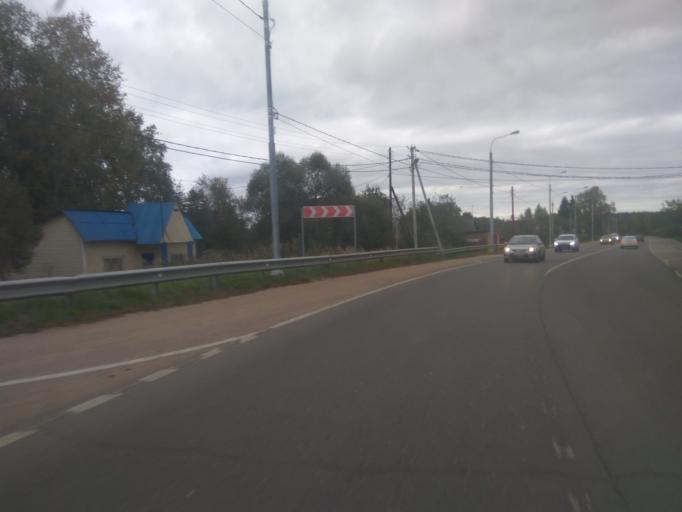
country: RU
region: Moskovskaya
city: Chupryakovo
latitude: 55.5734
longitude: 36.6587
